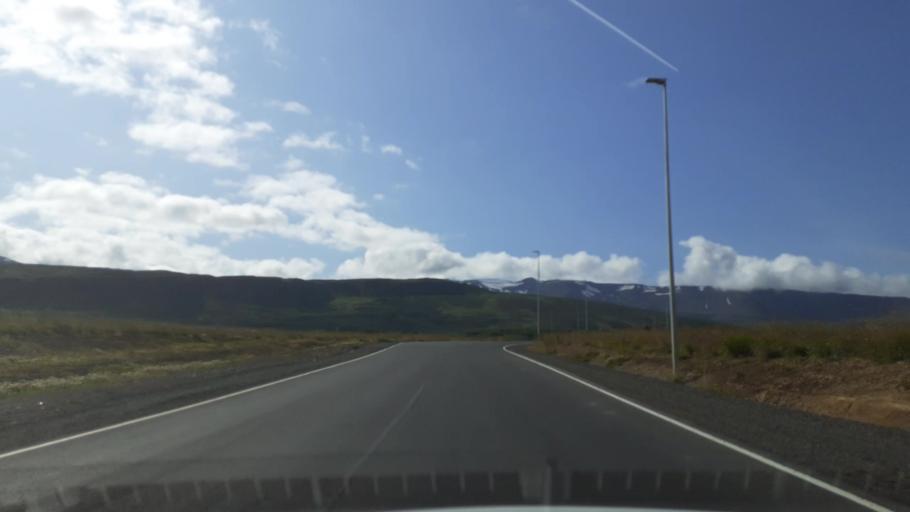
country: IS
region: Northeast
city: Akureyri
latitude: 65.6565
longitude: -18.0908
